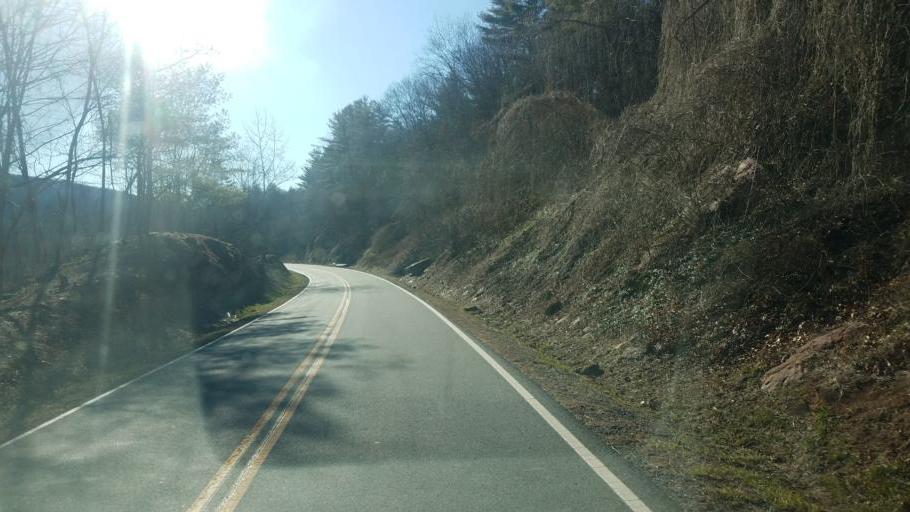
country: US
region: Virginia
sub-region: Pulaski County
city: Pulaski
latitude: 37.1726
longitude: -80.8880
